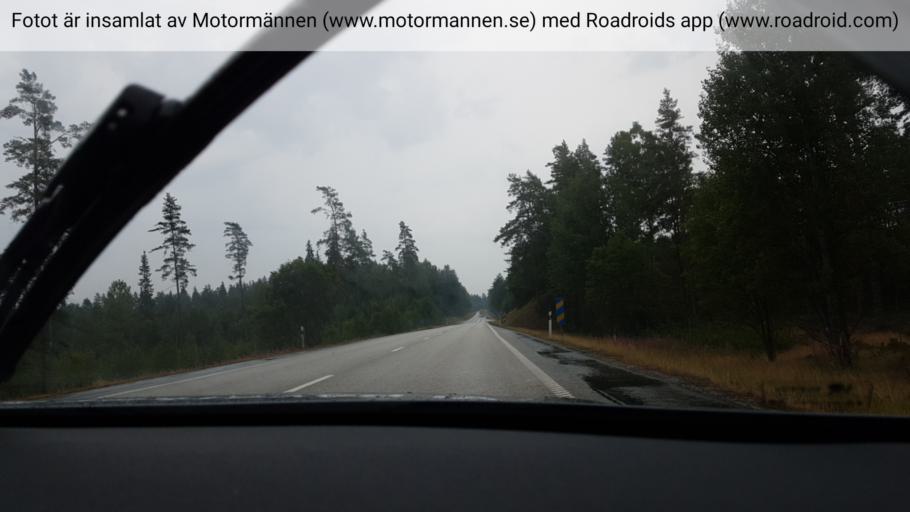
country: SE
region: Joenkoeping
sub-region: Jonkopings Kommun
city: Odensjo
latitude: 57.6134
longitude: 14.2067
